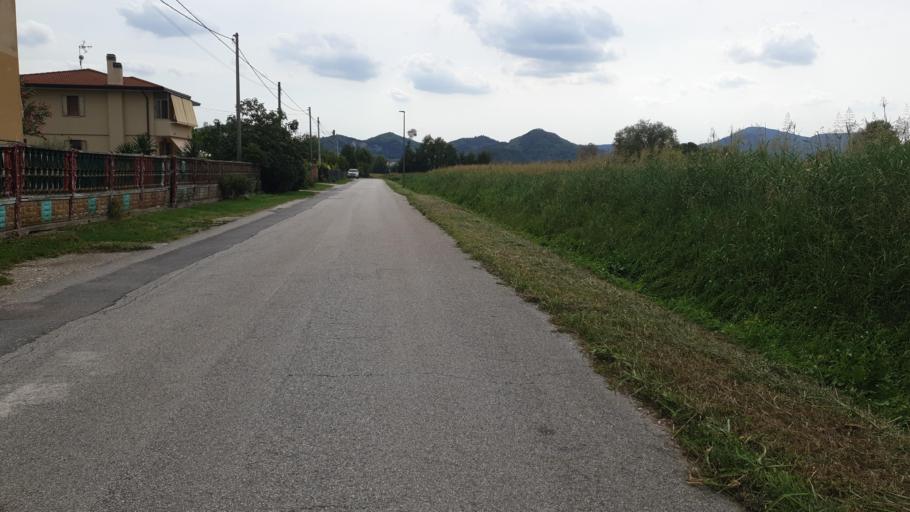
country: IT
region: Veneto
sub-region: Provincia di Padova
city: Montegrotto Terme
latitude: 45.3417
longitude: 11.8018
